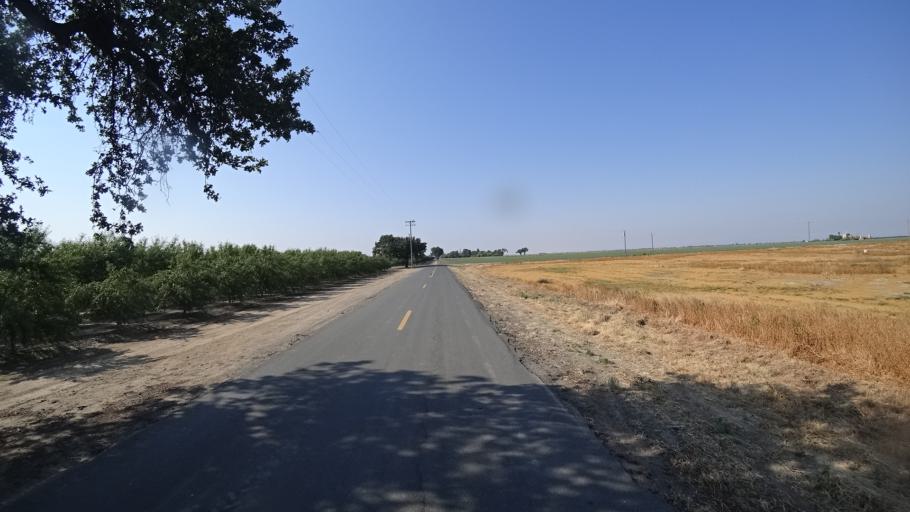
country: US
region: California
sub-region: Kings County
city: Lemoore
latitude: 36.3290
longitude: -119.8347
